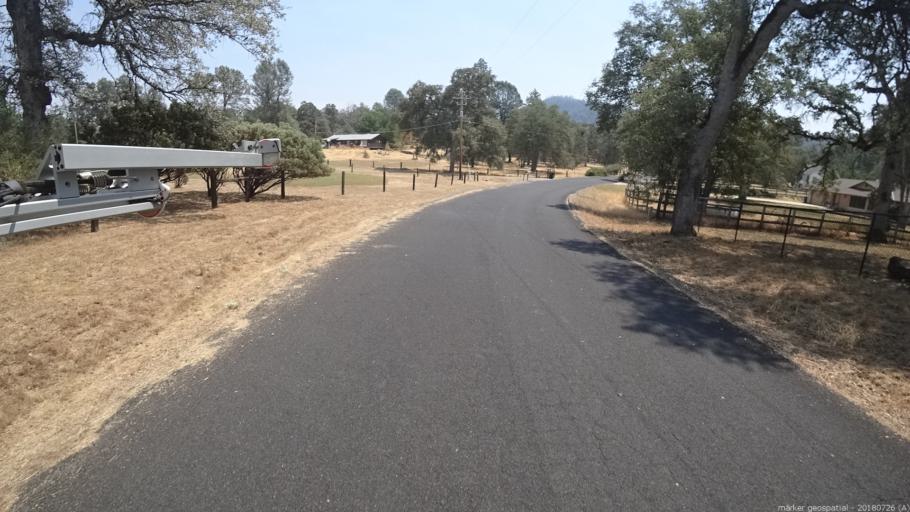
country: US
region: California
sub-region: Madera County
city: Oakhurst
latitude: 37.2850
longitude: -119.6354
